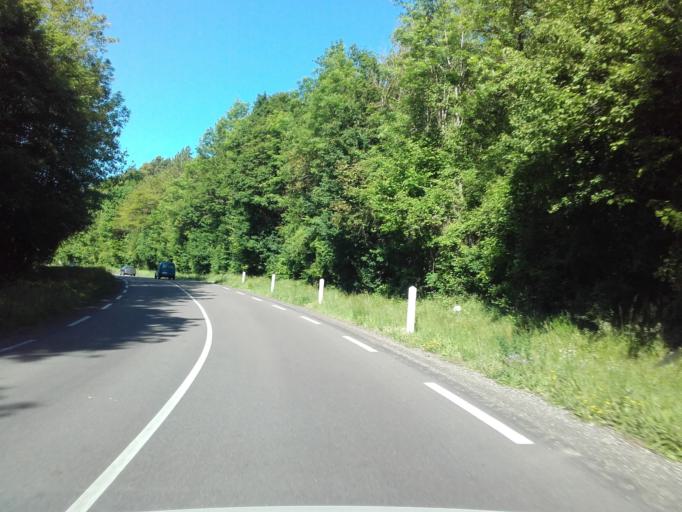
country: FR
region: Bourgogne
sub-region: Departement de la Cote-d'Or
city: Nolay
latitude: 46.9599
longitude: 4.6863
